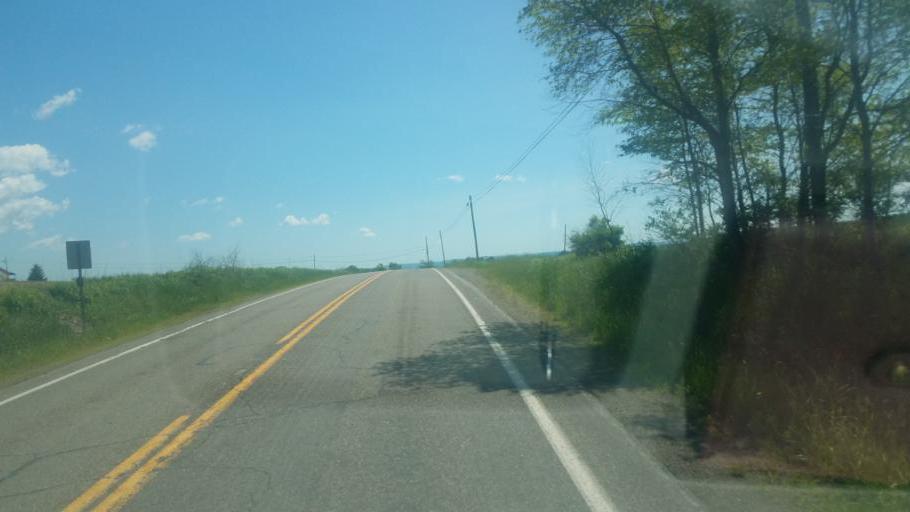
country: US
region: Pennsylvania
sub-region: Tioga County
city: Wellsboro
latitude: 41.7342
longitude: -77.3653
